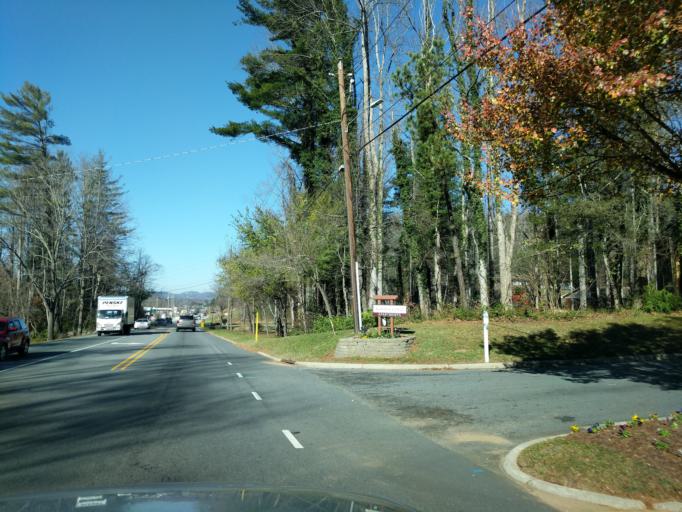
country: US
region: North Carolina
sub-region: Buncombe County
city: Biltmore Forest
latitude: 35.5313
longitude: -82.5183
